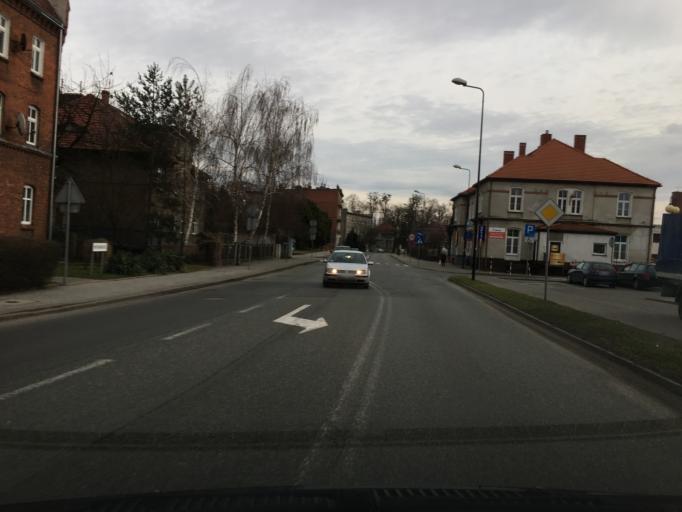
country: PL
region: Opole Voivodeship
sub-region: Powiat kedzierzynsko-kozielski
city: Kozle
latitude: 50.3326
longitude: 18.1487
